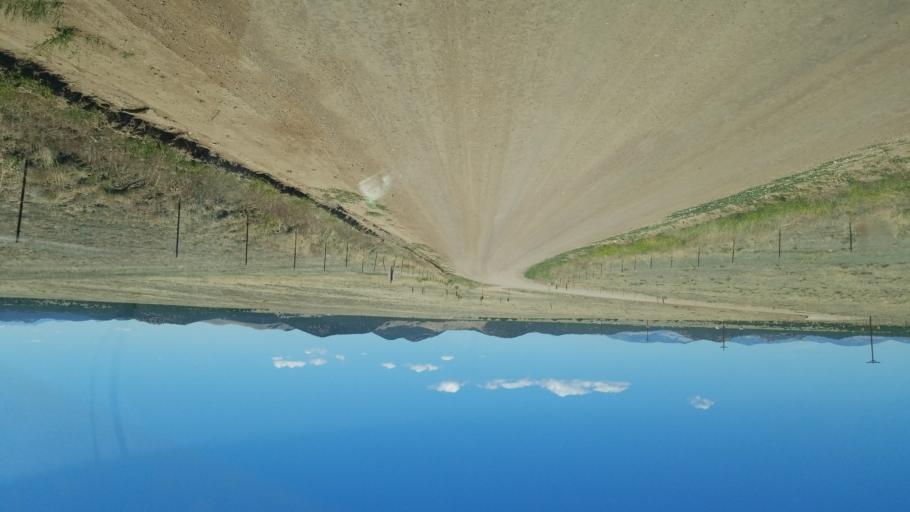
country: US
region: Colorado
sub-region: Custer County
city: Westcliffe
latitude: 38.2611
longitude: -105.4999
